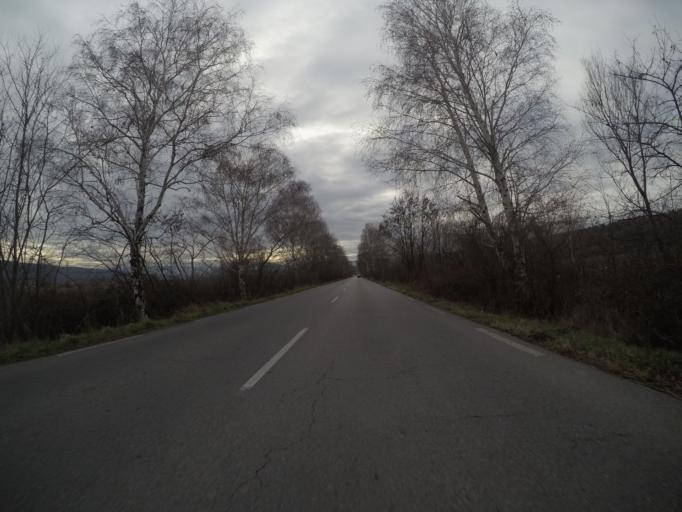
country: BG
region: Kyustendil
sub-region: Obshtina Rila
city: Rila
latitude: 42.1087
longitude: 23.1031
